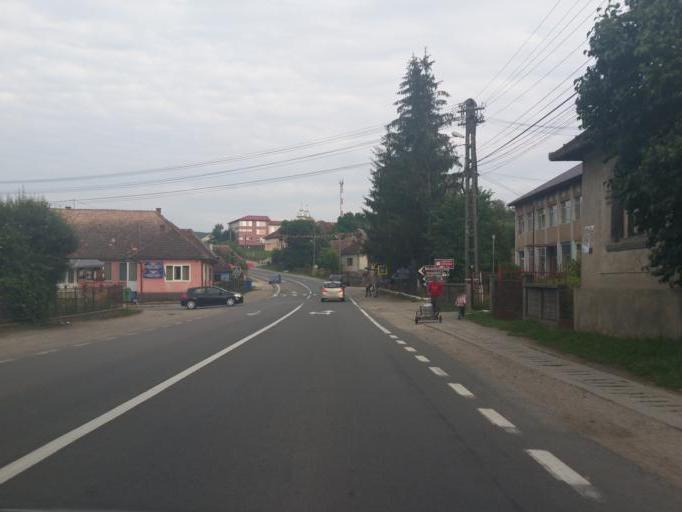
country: RO
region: Salaj
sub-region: Comuna Hida
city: Hida
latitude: 47.0373
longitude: 23.2663
